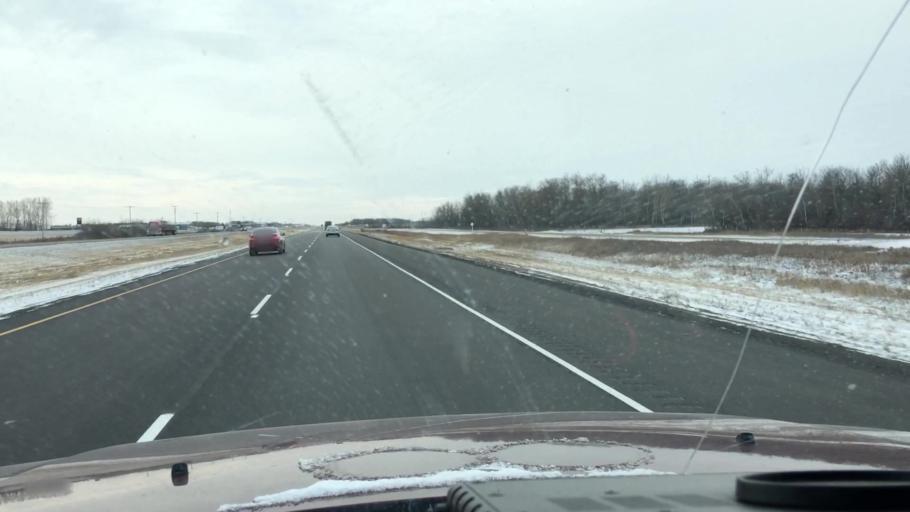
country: CA
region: Saskatchewan
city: Saskatoon
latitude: 51.9737
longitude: -106.5558
